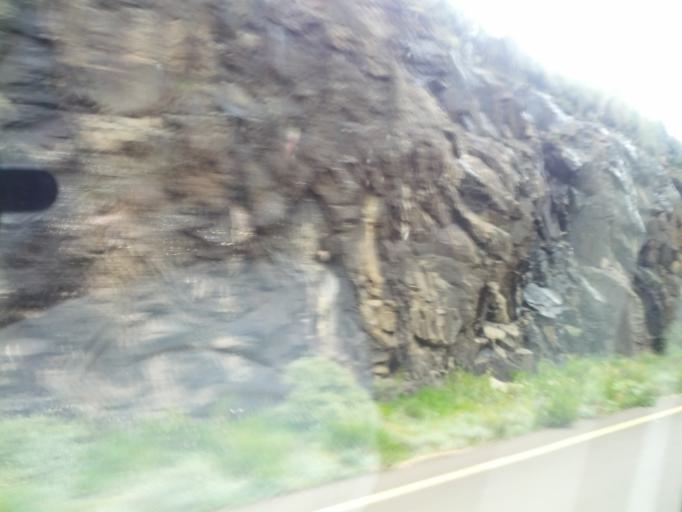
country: LS
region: Butha-Buthe
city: Butha-Buthe
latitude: -29.0638
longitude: 28.3711
